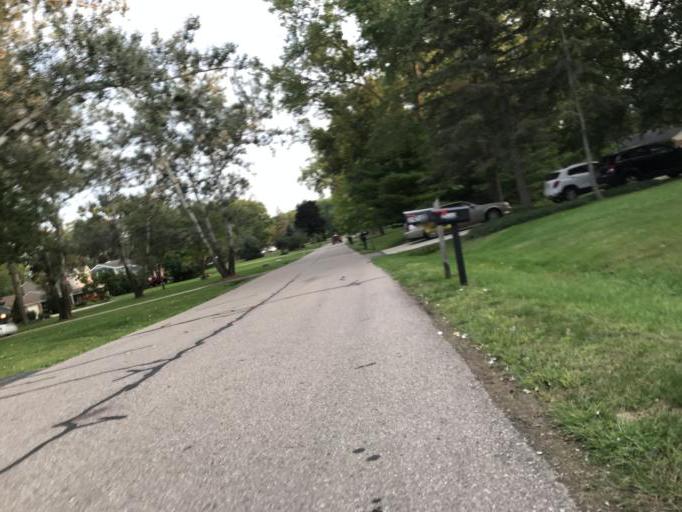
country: US
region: Michigan
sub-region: Oakland County
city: Farmington Hills
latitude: 42.4760
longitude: -83.3517
